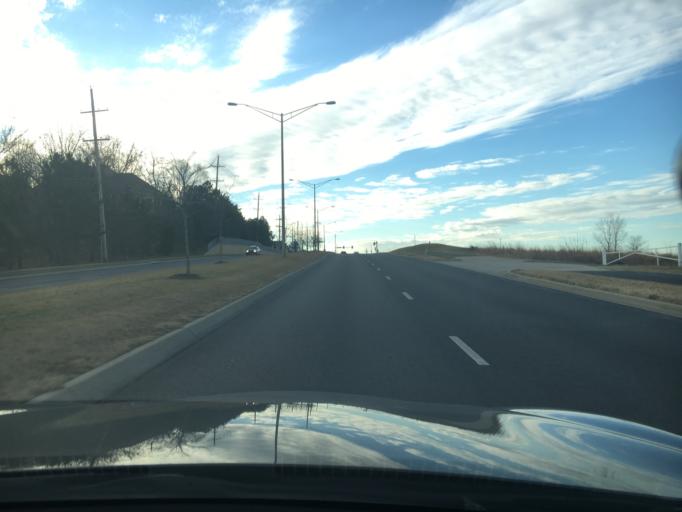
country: US
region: Kansas
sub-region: Johnson County
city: Lenexa
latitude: 38.8693
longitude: -94.6705
